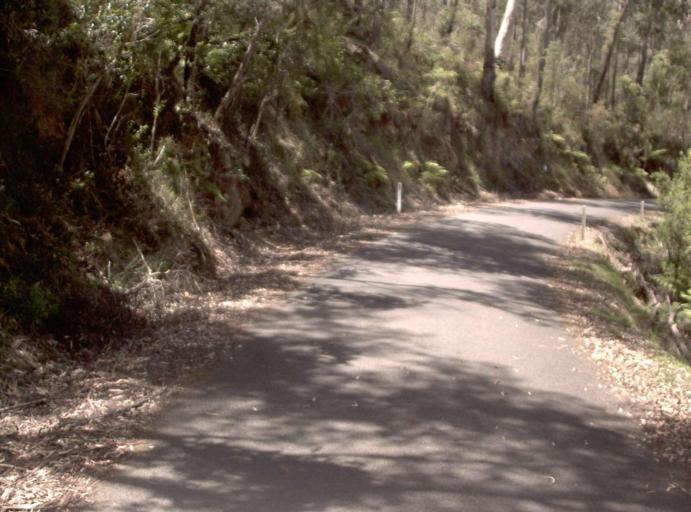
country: AU
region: New South Wales
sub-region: Bombala
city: Bombala
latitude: -37.4392
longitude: 148.9795
